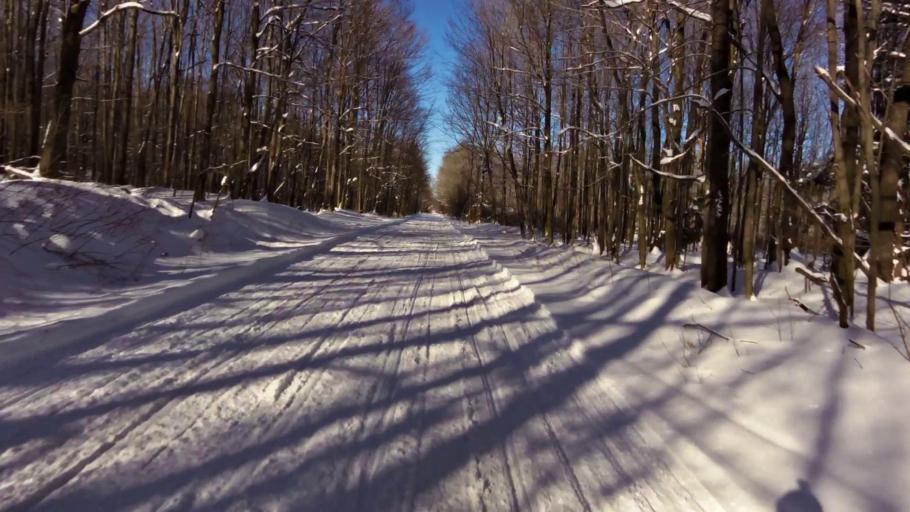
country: US
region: New York
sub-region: Chautauqua County
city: Mayville
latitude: 42.1825
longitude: -79.5802
